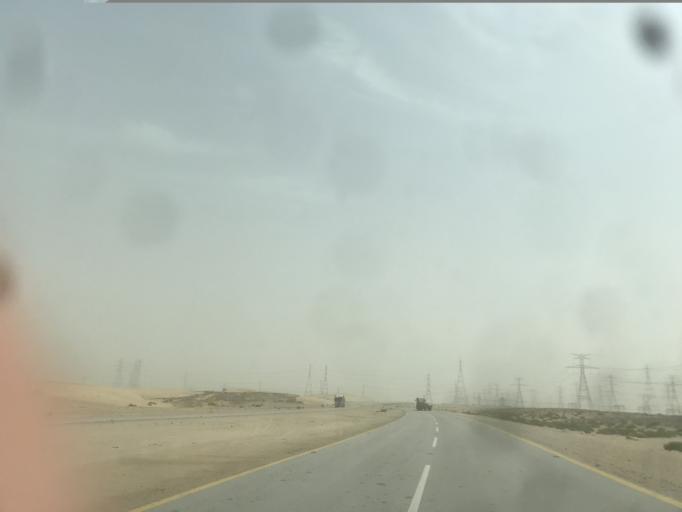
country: SA
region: Eastern Province
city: Abqaiq
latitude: 25.9074
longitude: 49.8916
